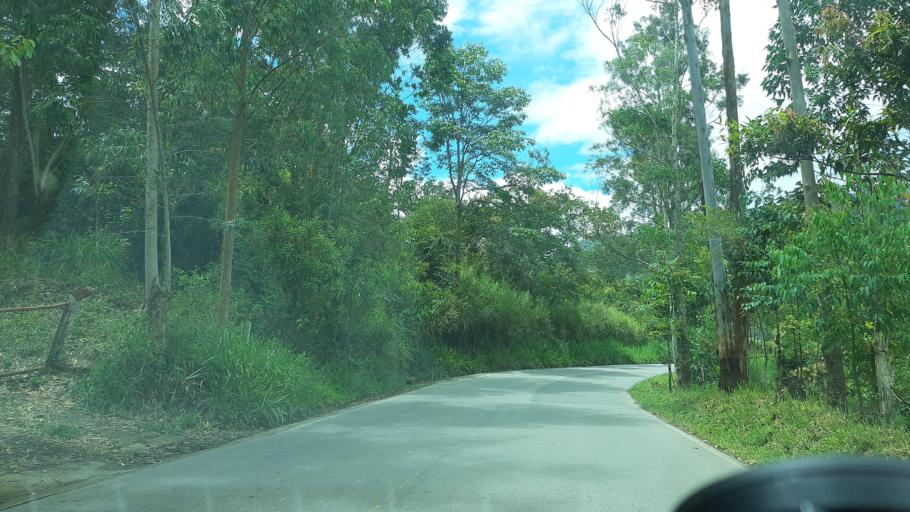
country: CO
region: Boyaca
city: Garagoa
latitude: 5.0524
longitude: -73.3862
